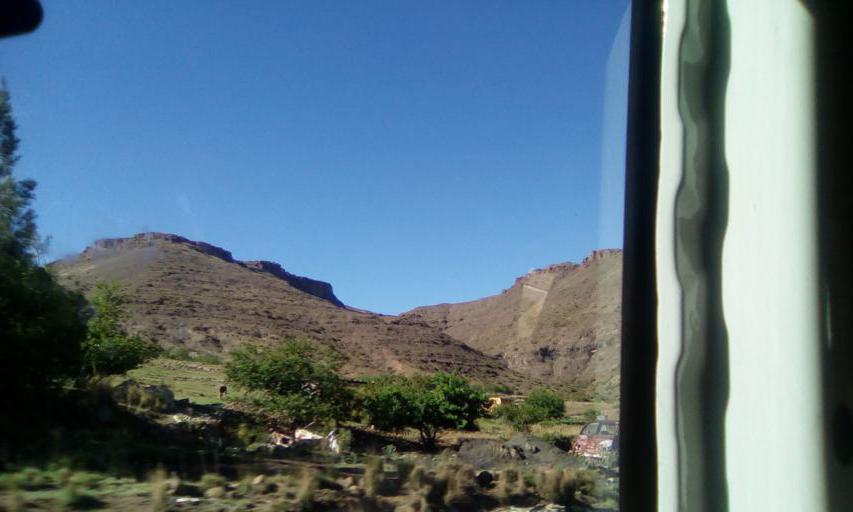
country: LS
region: Qacha's Nek
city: Qacha's Nek
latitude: -30.0574
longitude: 28.2870
